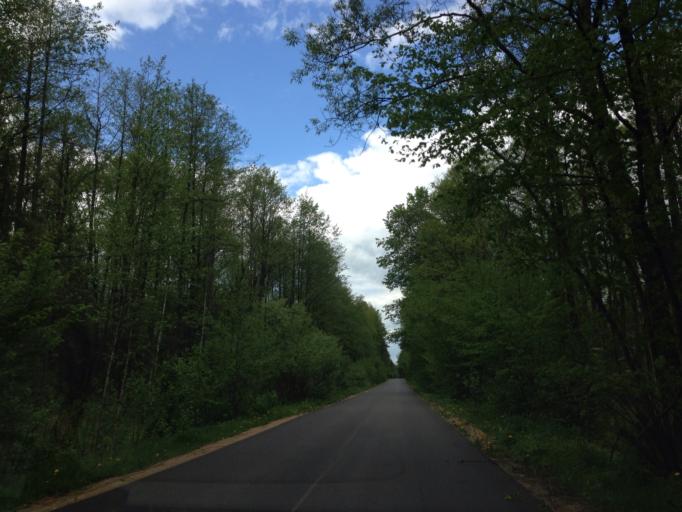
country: PL
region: Podlasie
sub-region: Powiat grajewski
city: Radzilow
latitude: 53.3312
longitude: 22.5998
